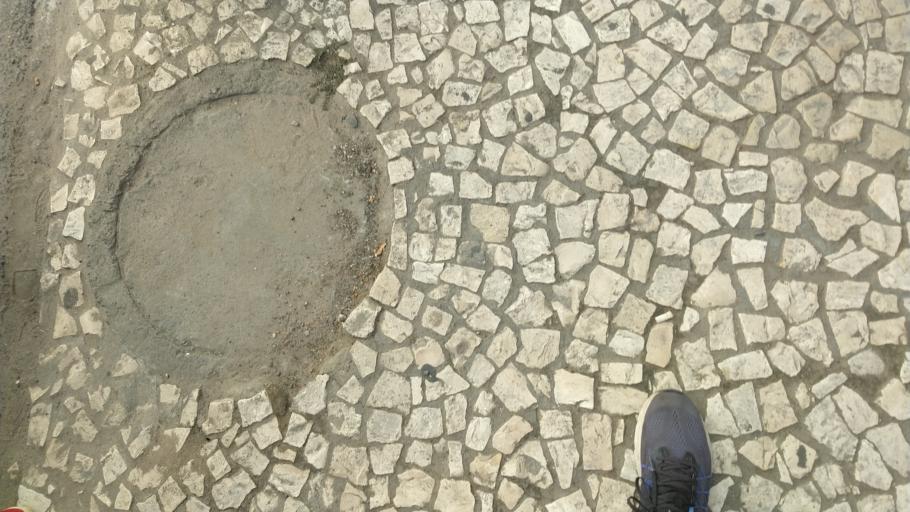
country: BR
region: Bahia
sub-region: Feira De Santana
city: Feira de Santana
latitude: -12.2565
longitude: -38.9549
